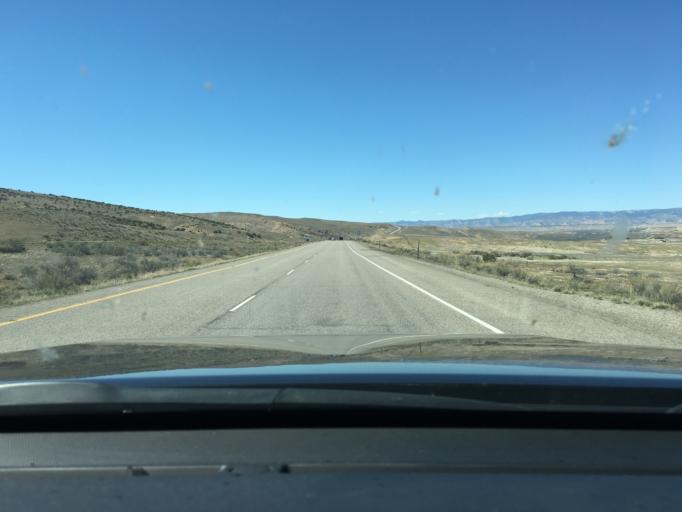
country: US
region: Colorado
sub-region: Mesa County
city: Loma
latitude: 39.2169
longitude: -108.8731
